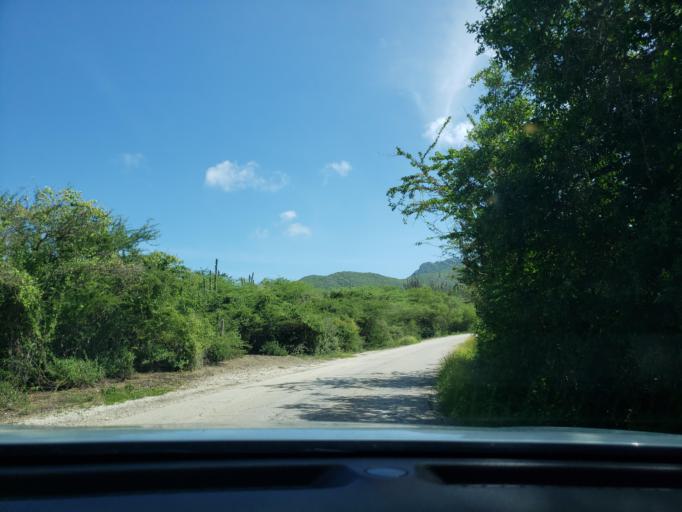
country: CW
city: Dorp Soto
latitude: 12.3534
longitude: -69.1471
